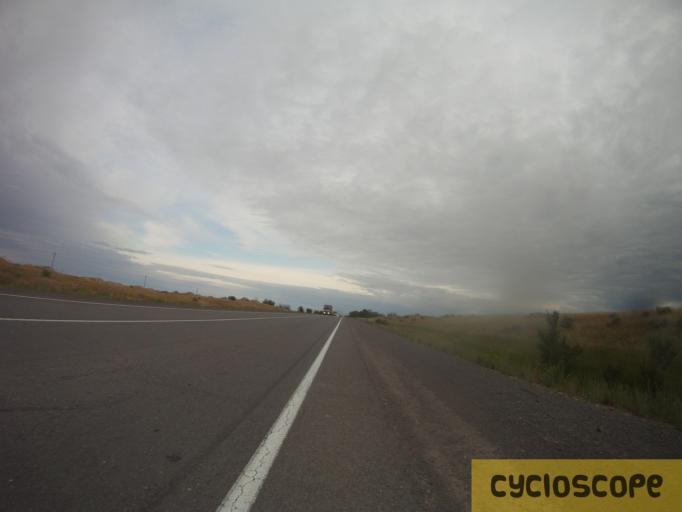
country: KG
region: Chuy
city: Tokmok
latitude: 43.3676
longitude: 75.3230
